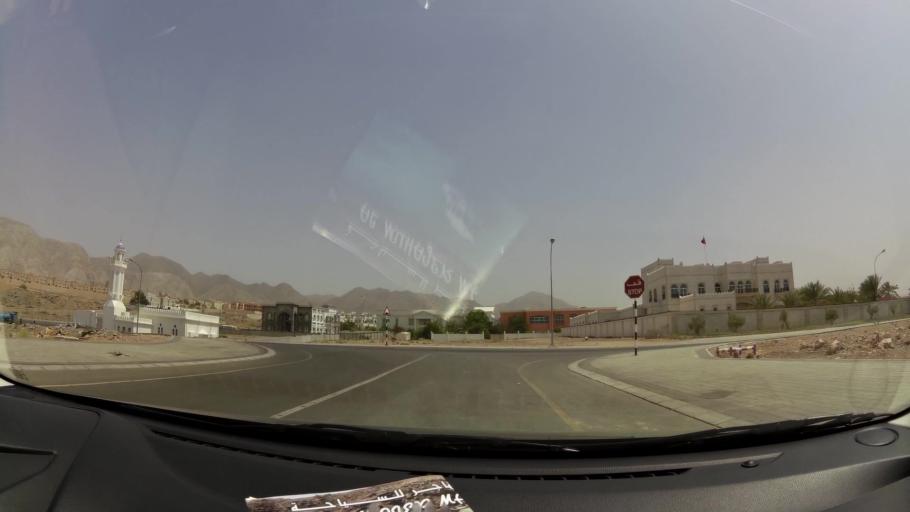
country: OM
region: Muhafazat Masqat
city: Bawshar
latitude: 23.5622
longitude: 58.3957
